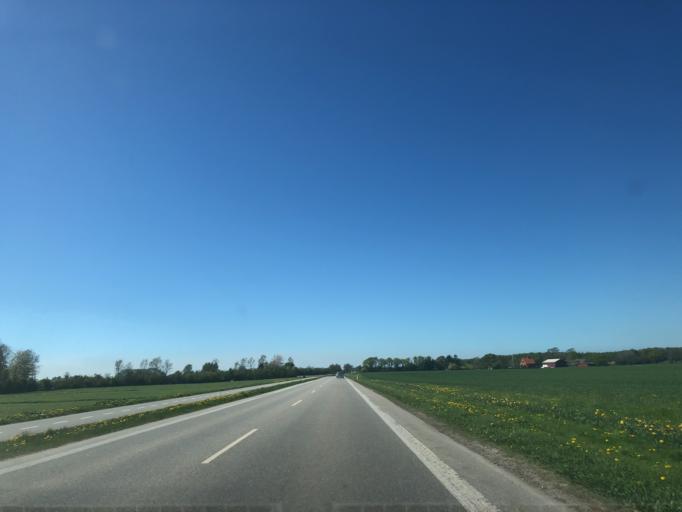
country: DK
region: Zealand
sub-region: Stevns Kommune
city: Store Heddinge
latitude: 55.3320
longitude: 12.3582
